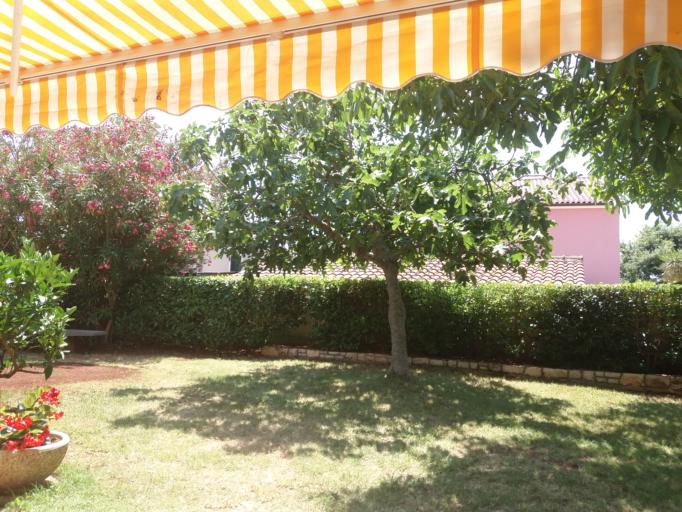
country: HR
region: Istarska
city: Medulin
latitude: 44.8034
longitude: 13.9167
